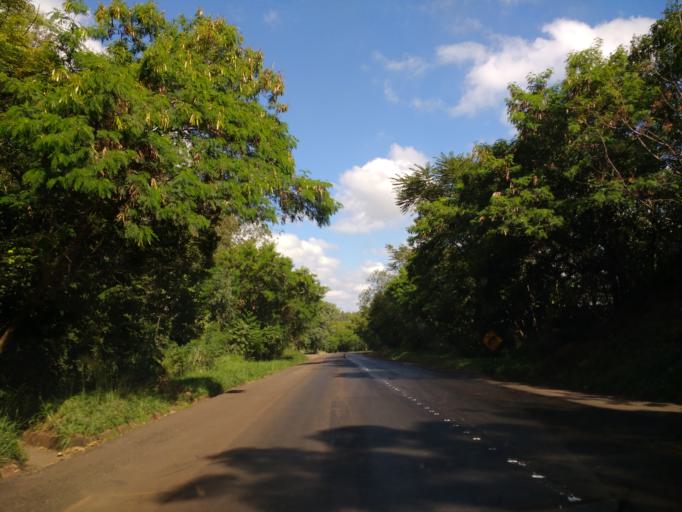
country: BR
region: Parana
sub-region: Umuarama
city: Umuarama
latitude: -23.8763
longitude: -53.3952
